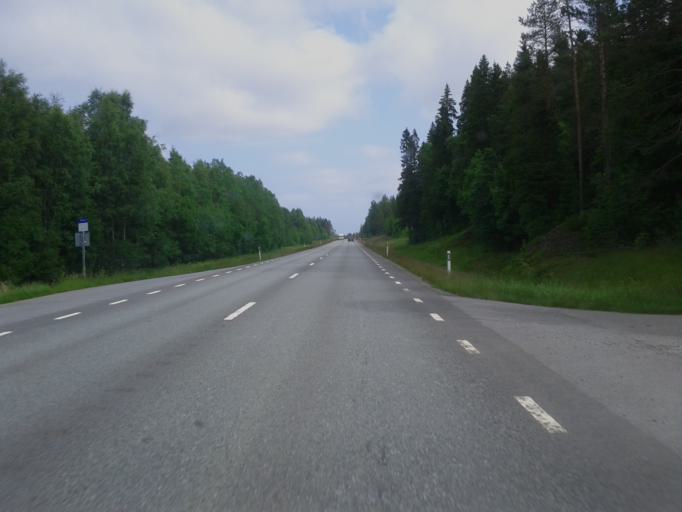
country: SE
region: Vaesterbotten
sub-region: Skelleftea Kommun
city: Burea
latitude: 64.3397
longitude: 21.2769
